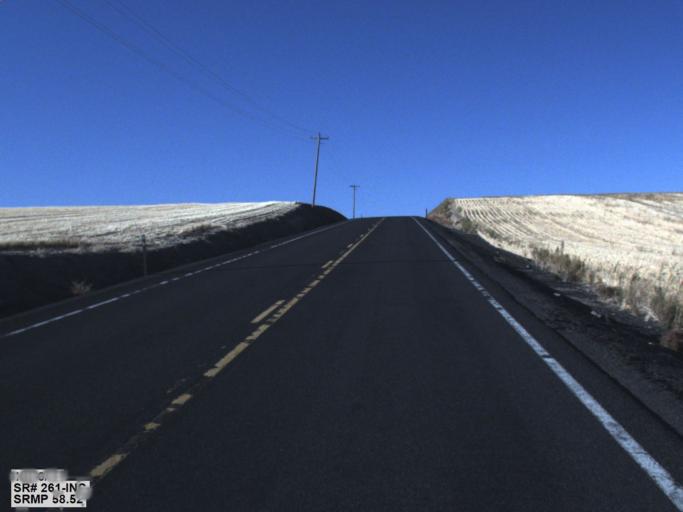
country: US
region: Washington
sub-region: Adams County
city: Ritzville
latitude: 47.0555
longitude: -118.3612
